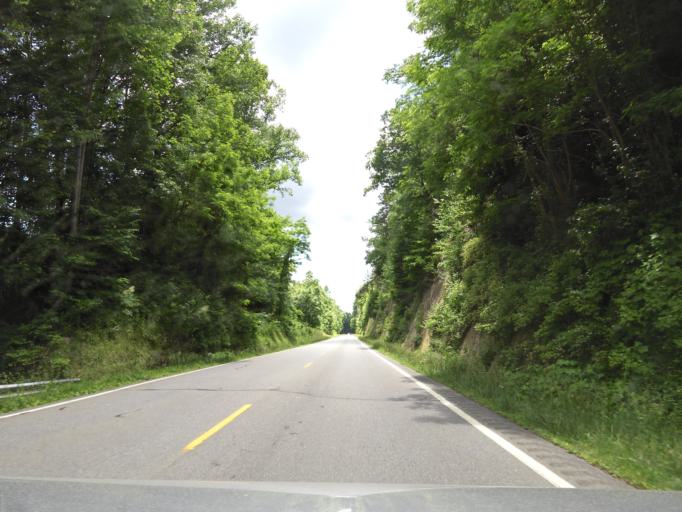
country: US
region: North Carolina
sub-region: Graham County
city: Robbinsville
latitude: 35.2609
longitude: -83.6968
